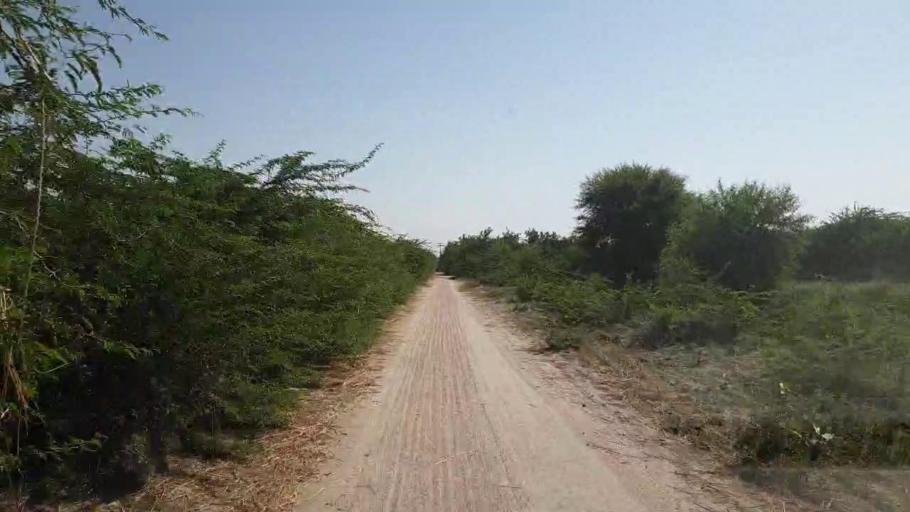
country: PK
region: Sindh
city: Tando Bago
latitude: 24.6472
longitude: 68.9856
